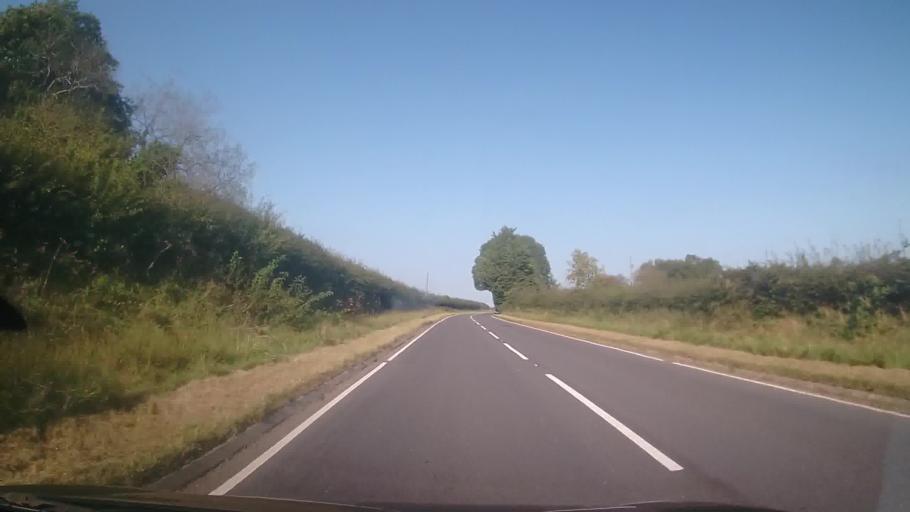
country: GB
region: Wales
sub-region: County of Ceredigion
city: Llangybi
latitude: 52.1623
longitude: -4.0309
